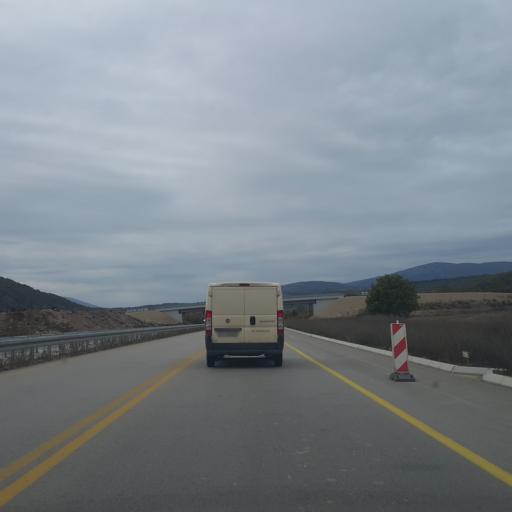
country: RS
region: Central Serbia
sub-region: Pirotski Okrug
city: Pirot
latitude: 43.2241
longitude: 22.4769
